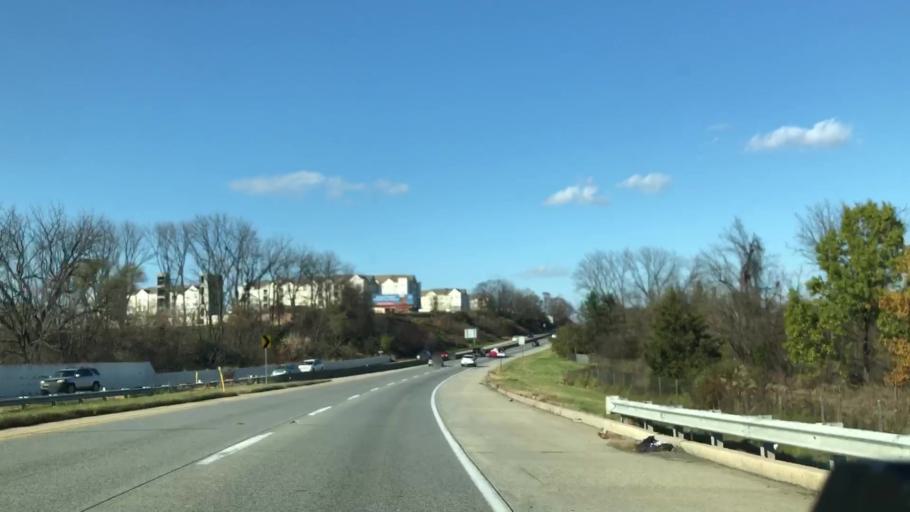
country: US
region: Pennsylvania
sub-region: Lehigh County
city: Wescosville
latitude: 40.5794
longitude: -75.5521
